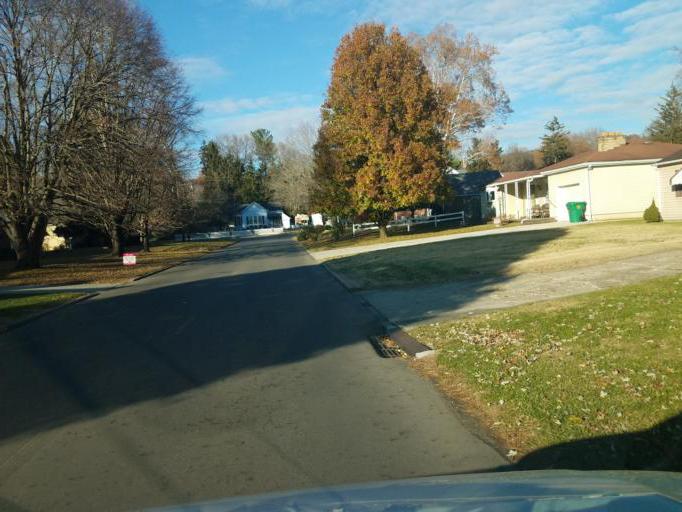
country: US
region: Ohio
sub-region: Scioto County
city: Rosemount
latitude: 38.7553
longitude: -82.9747
